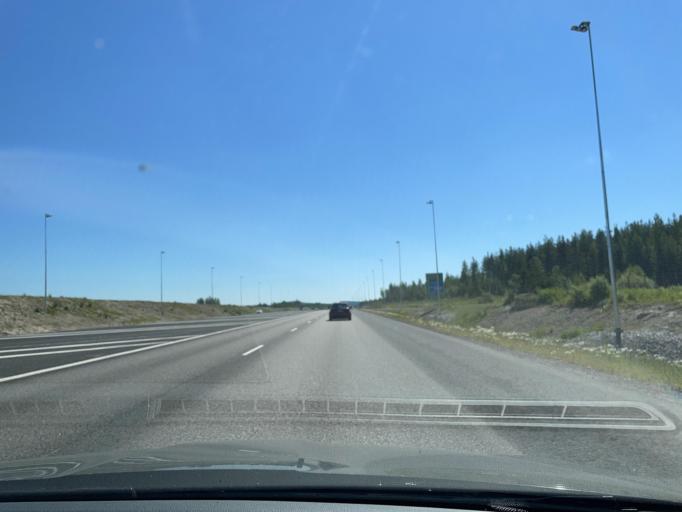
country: FI
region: Central Finland
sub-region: Jyvaeskylae
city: Jyvaeskylae
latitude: 62.4001
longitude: 25.7012
